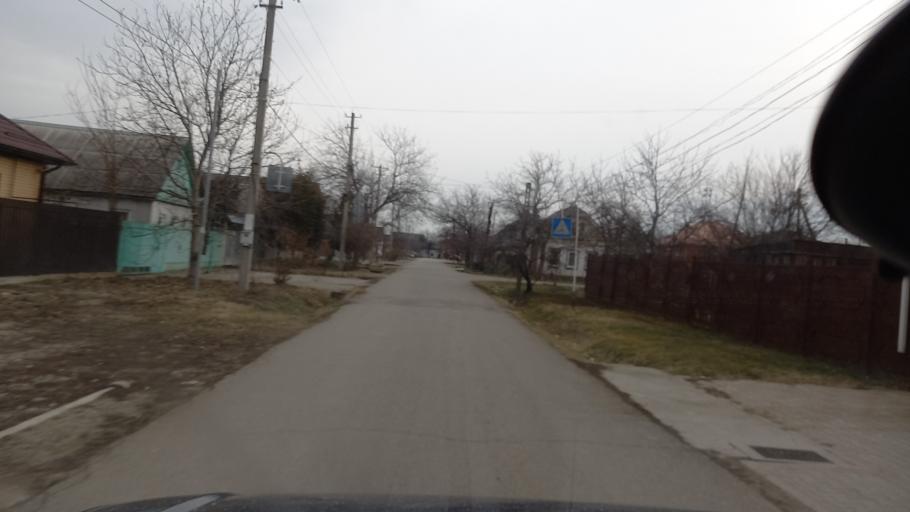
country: RU
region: Adygeya
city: Maykop
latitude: 44.5914
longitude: 40.0986
